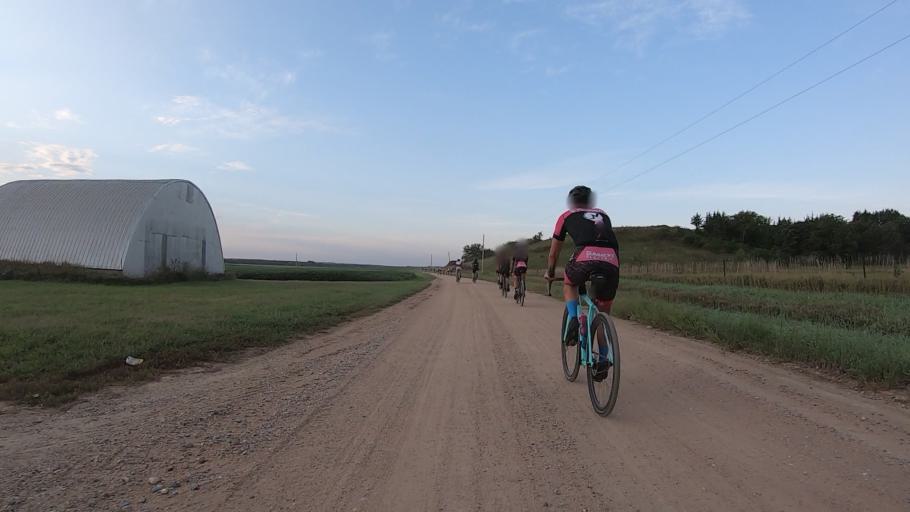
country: US
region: Kansas
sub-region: Marshall County
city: Marysville
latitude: 39.8274
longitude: -96.6655
